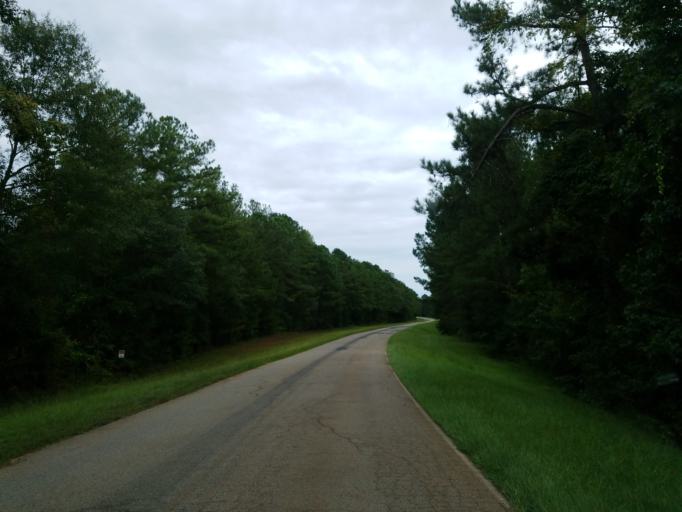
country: US
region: Georgia
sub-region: Monroe County
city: Forsyth
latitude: 32.9583
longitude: -83.9621
